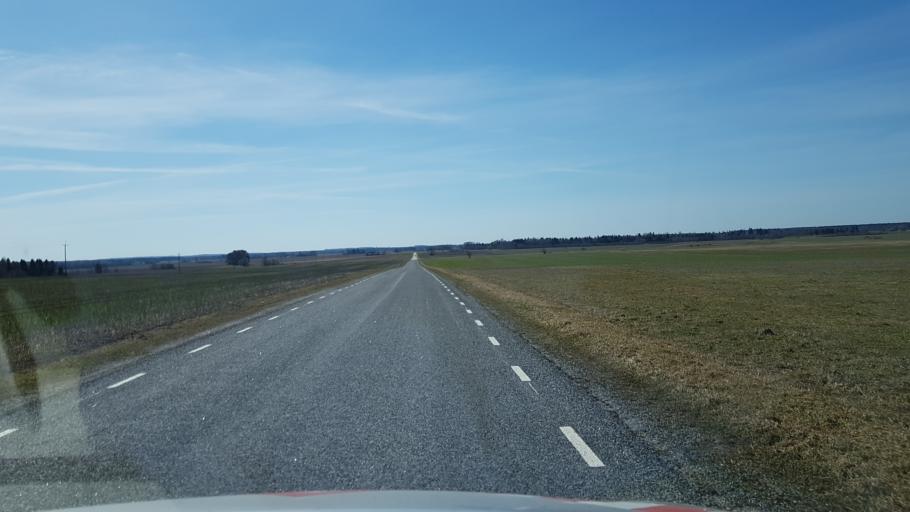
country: EE
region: Laeaene-Virumaa
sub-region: Vinni vald
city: Vinni
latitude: 59.0900
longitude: 26.4707
